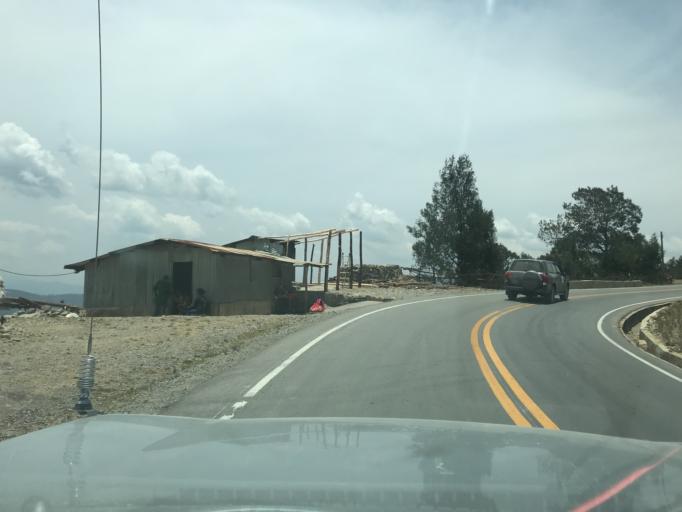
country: TL
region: Manufahi
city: Same
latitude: -8.8778
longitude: 125.5986
